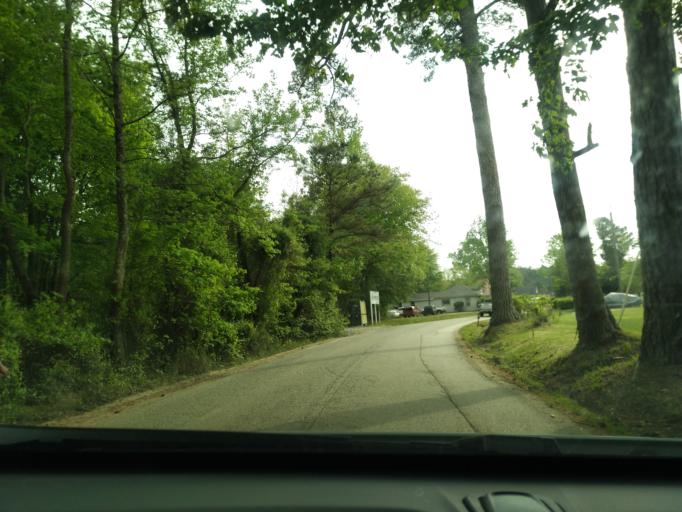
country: US
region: Virginia
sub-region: York County
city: Yorktown
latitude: 37.1689
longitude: -76.5175
